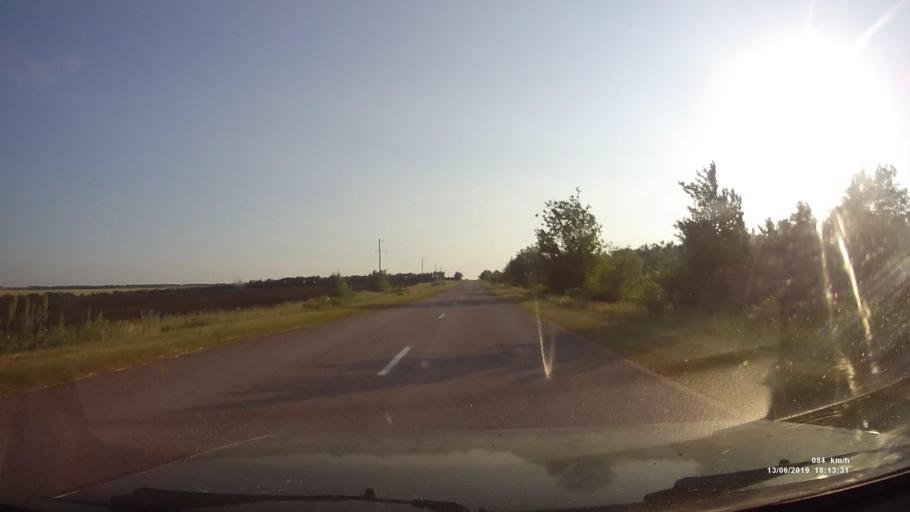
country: RU
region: Rostov
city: Kazanskaya
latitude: 49.9384
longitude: 41.3931
